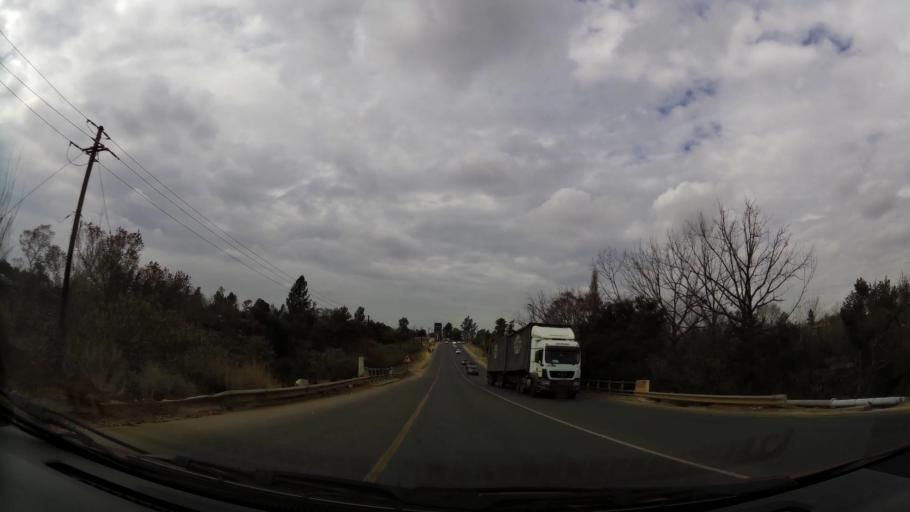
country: ZA
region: Gauteng
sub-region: West Rand District Municipality
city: Muldersdriseloop
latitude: -26.0629
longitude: 27.8414
